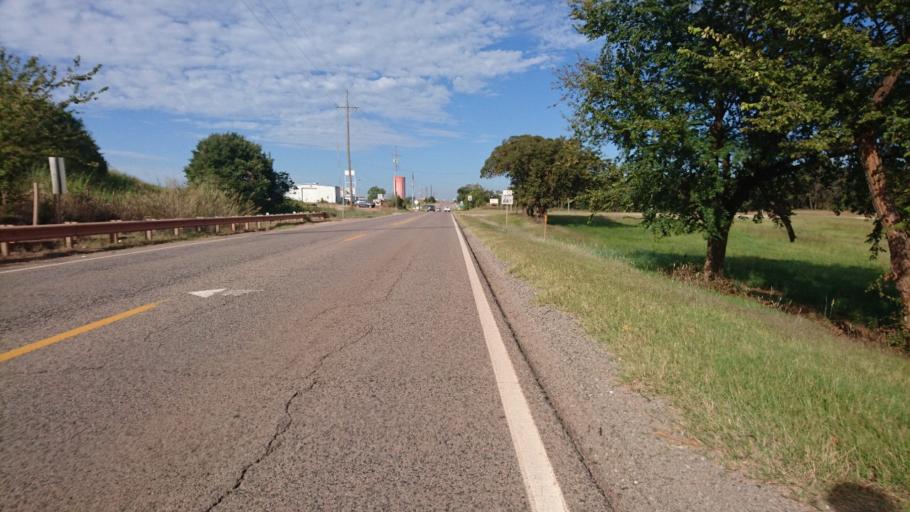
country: US
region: Oklahoma
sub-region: Oklahoma County
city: Luther
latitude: 35.6811
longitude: -97.0482
